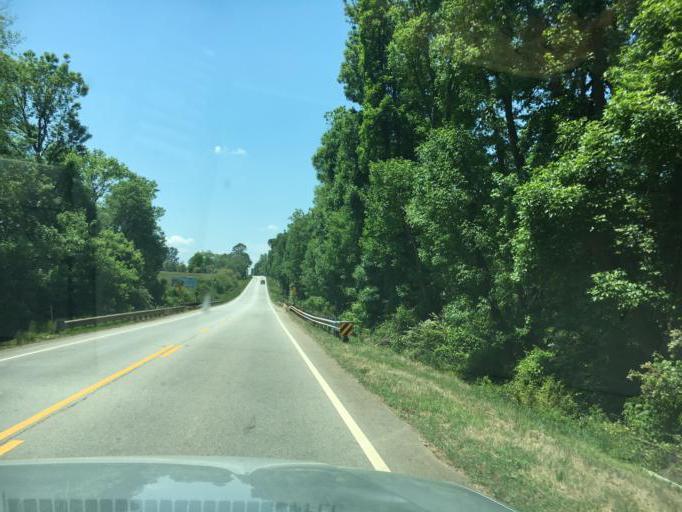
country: US
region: Georgia
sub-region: Hart County
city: Royston
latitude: 34.2897
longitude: -83.0784
